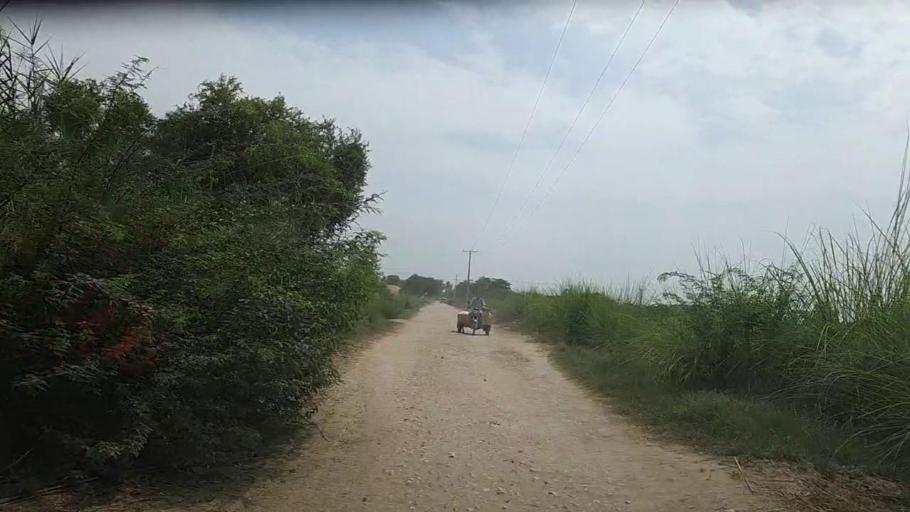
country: PK
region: Sindh
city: Bhiria
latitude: 26.8855
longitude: 68.2954
